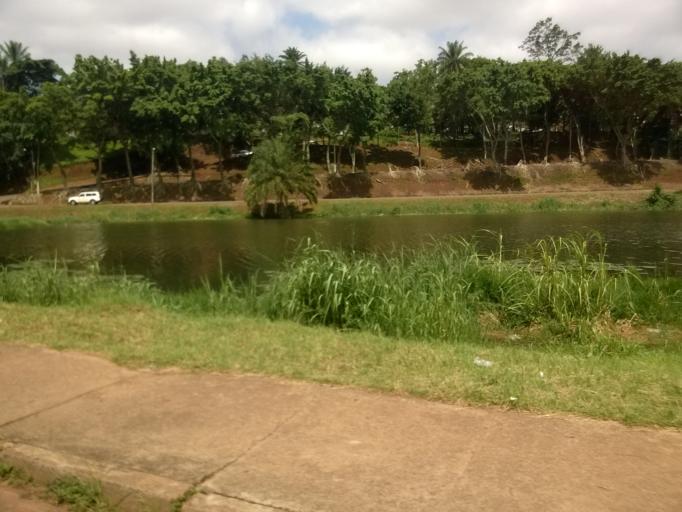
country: CM
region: Centre
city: Yaounde
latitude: 3.8628
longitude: 11.5119
